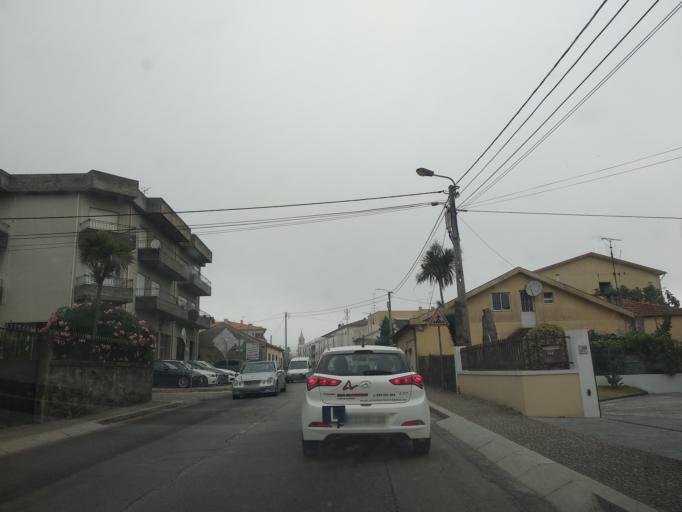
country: PT
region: Braga
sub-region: Vila Verde
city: Vila Verde
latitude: 41.6435
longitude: -8.4354
